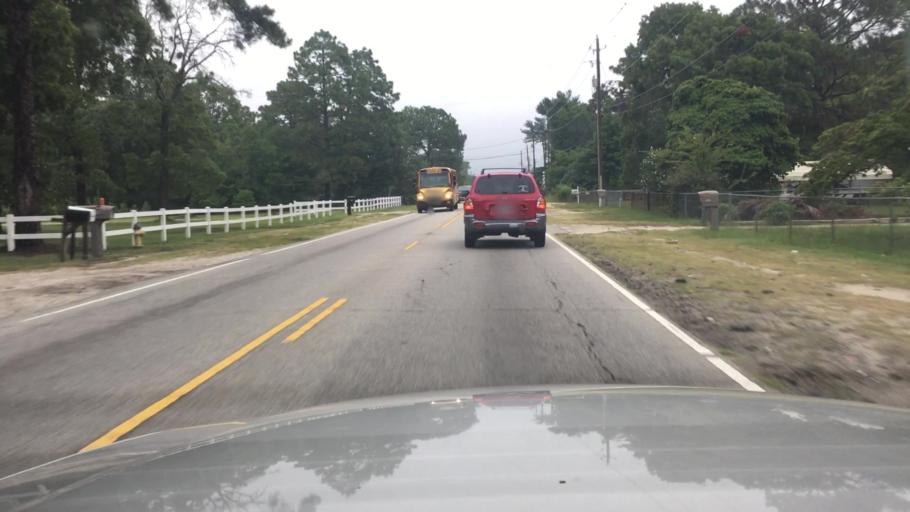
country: US
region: North Carolina
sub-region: Cumberland County
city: Hope Mills
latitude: 34.9785
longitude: -78.9825
